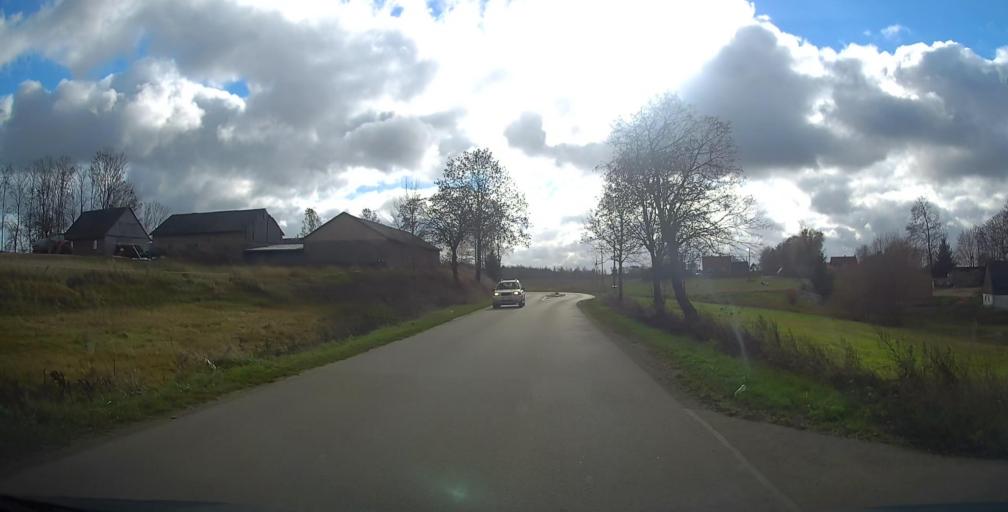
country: PL
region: Podlasie
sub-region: Suwalki
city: Suwalki
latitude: 54.3180
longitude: 22.8636
